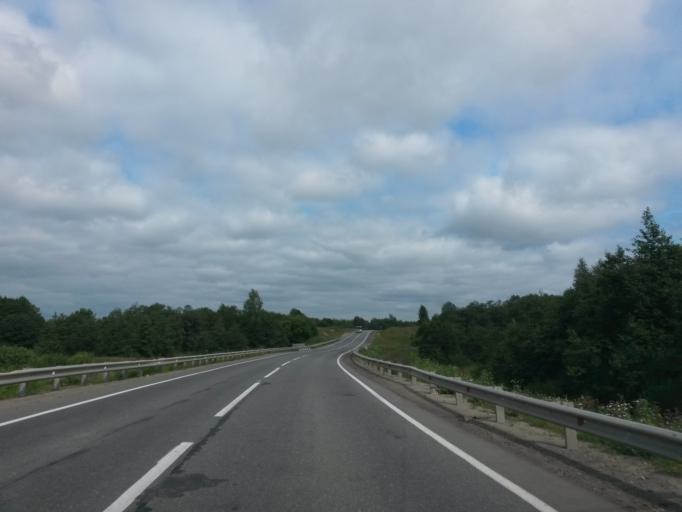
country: RU
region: Jaroslavl
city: Gavrilov-Yam
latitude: 57.3280
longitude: 39.9216
